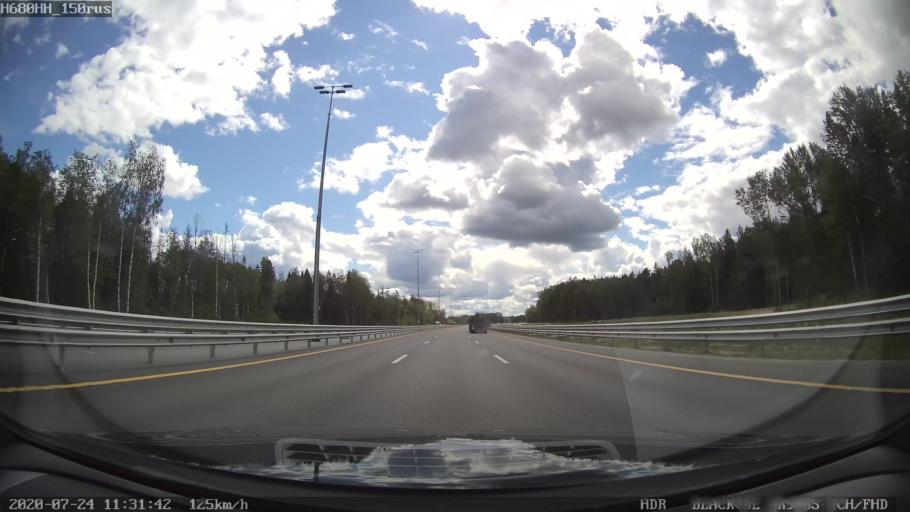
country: RU
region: Leningrad
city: Krasnyy Bor
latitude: 59.6530
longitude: 30.6436
